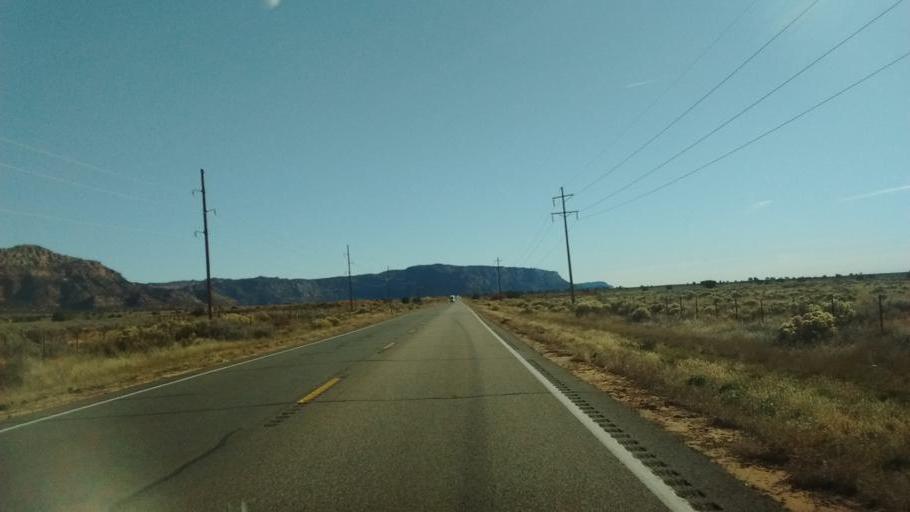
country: US
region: Arizona
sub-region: Mohave County
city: Colorado City
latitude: 37.0163
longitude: -113.0273
